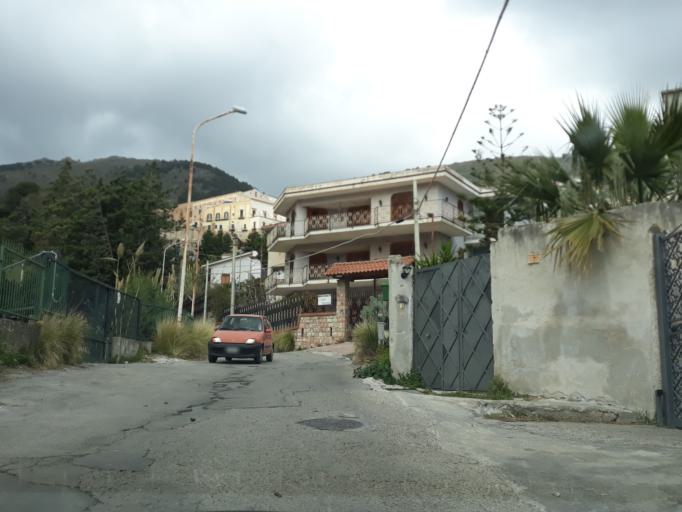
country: IT
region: Sicily
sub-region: Palermo
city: Monreale
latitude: 38.0802
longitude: 13.2963
